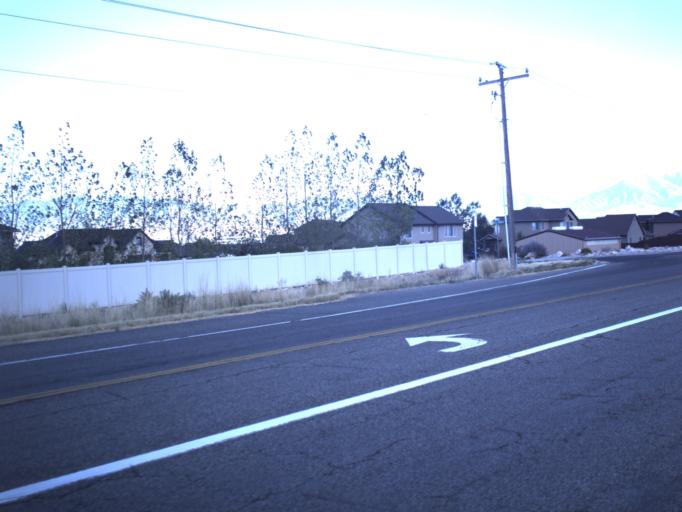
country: US
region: Utah
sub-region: Tooele County
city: Grantsville
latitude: 40.6199
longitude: -112.5025
